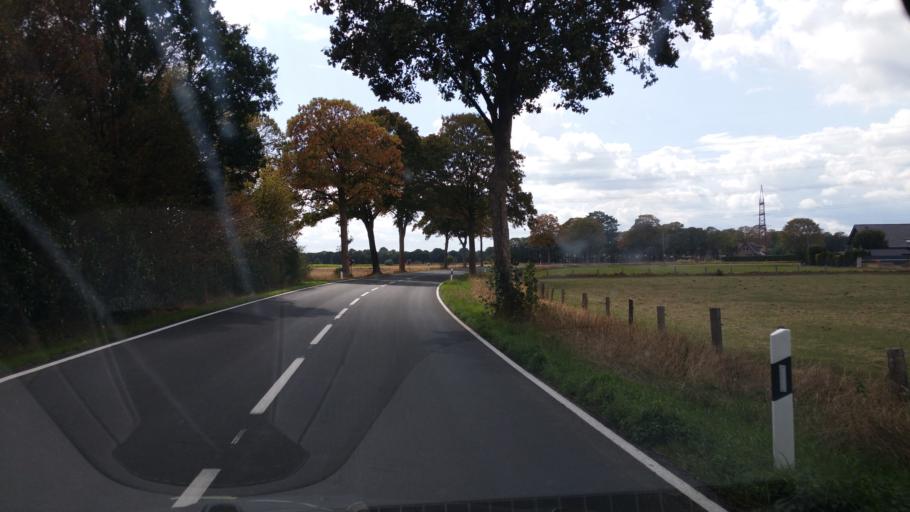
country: DE
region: North Rhine-Westphalia
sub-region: Regierungsbezirk Dusseldorf
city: Hamminkeln
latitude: 51.7176
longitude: 6.5840
